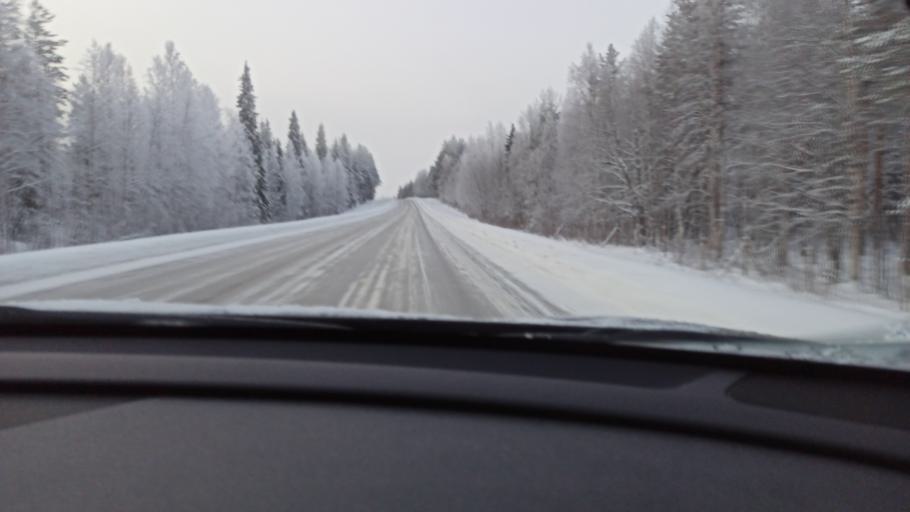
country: FI
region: Lapland
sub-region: Pohjois-Lappi
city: Sodankylae
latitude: 66.9975
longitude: 26.3659
